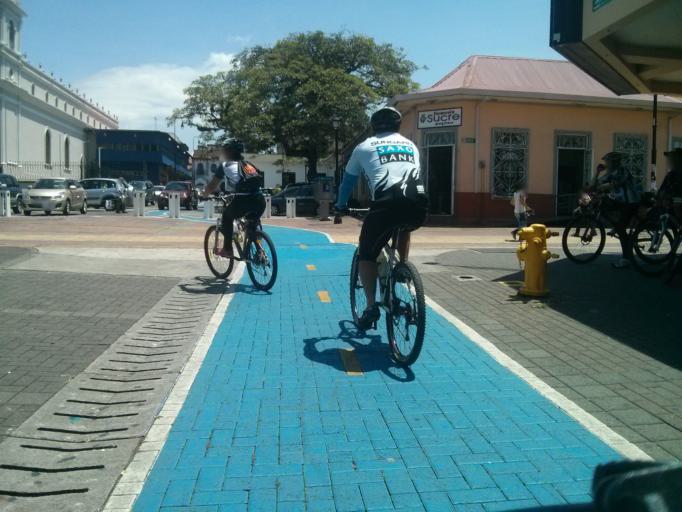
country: CR
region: San Jose
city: San Jose
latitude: 9.9316
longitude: -84.0753
